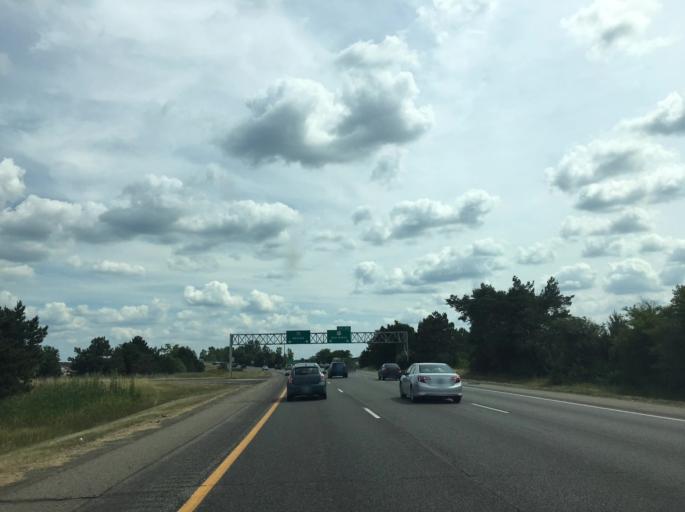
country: US
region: Michigan
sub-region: Genesee County
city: Flint
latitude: 42.9568
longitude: -83.7253
